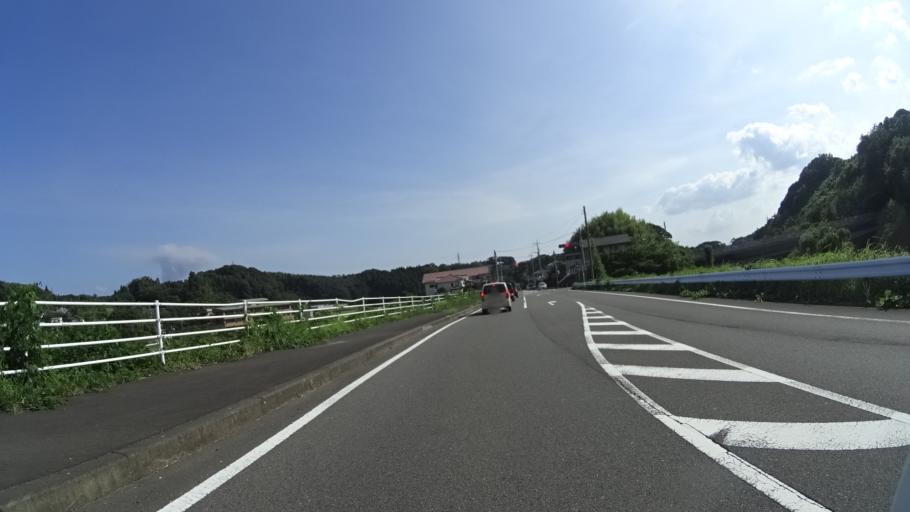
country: JP
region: Kagoshima
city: Kagoshima-shi
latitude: 31.6528
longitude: 130.5522
